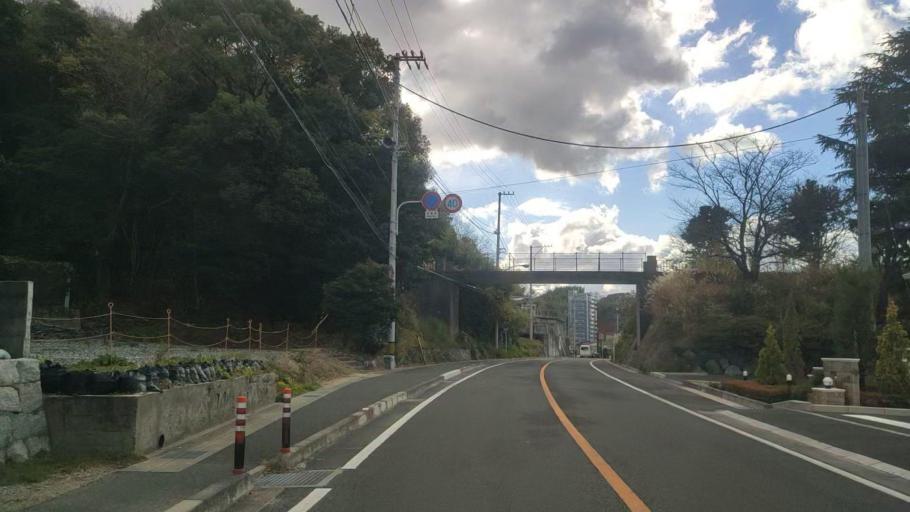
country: JP
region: Ehime
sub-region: Shikoku-chuo Shi
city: Matsuyama
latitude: 33.8739
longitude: 132.7089
